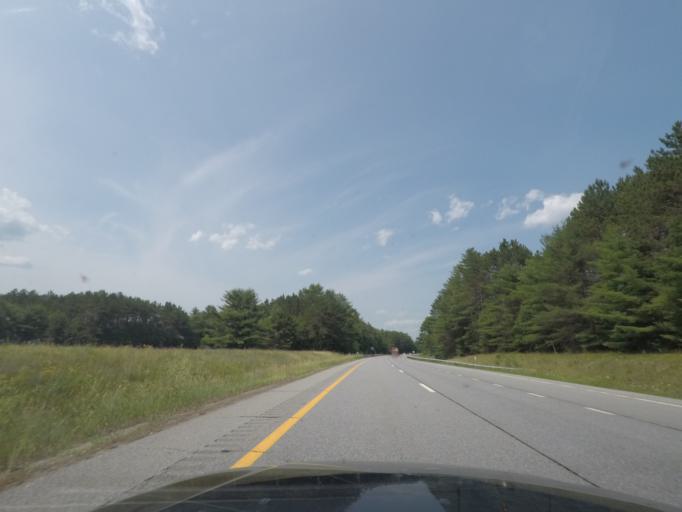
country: US
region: New York
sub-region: Warren County
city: Warrensburg
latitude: 43.5528
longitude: -73.7351
